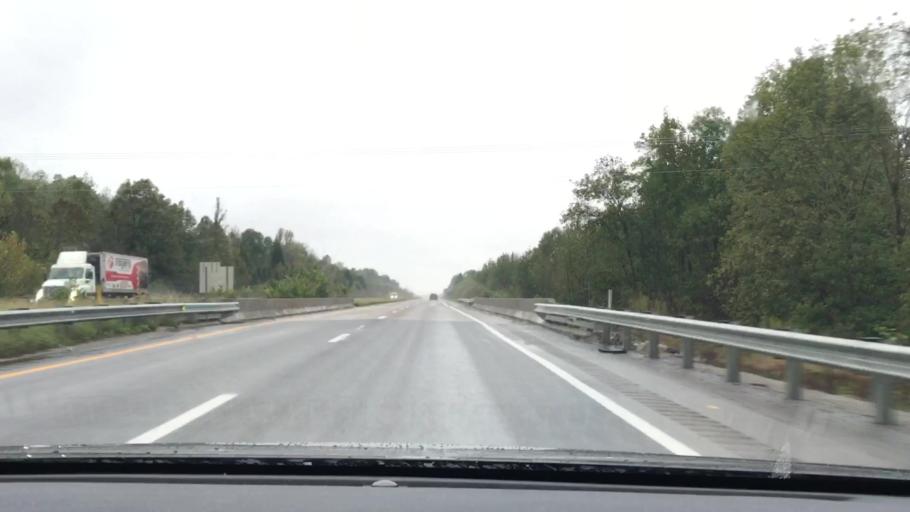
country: US
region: Kentucky
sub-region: Hopkins County
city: Nortonville
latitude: 37.1849
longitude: -87.4446
